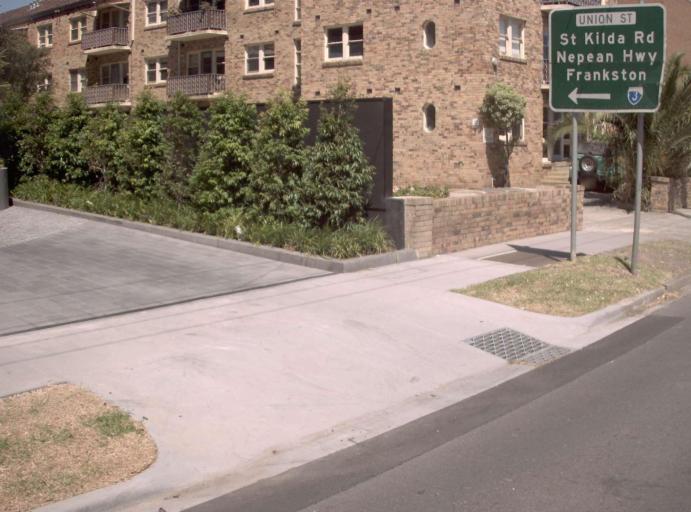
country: AU
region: Victoria
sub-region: Port Phillip
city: St Kilda West
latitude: -37.8525
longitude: 144.9791
